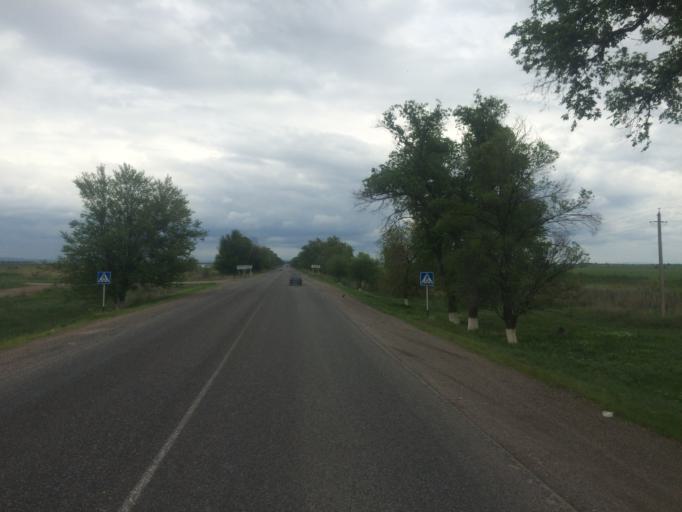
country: KZ
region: Zhambyl
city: Georgiyevka
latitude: 43.2263
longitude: 74.4050
